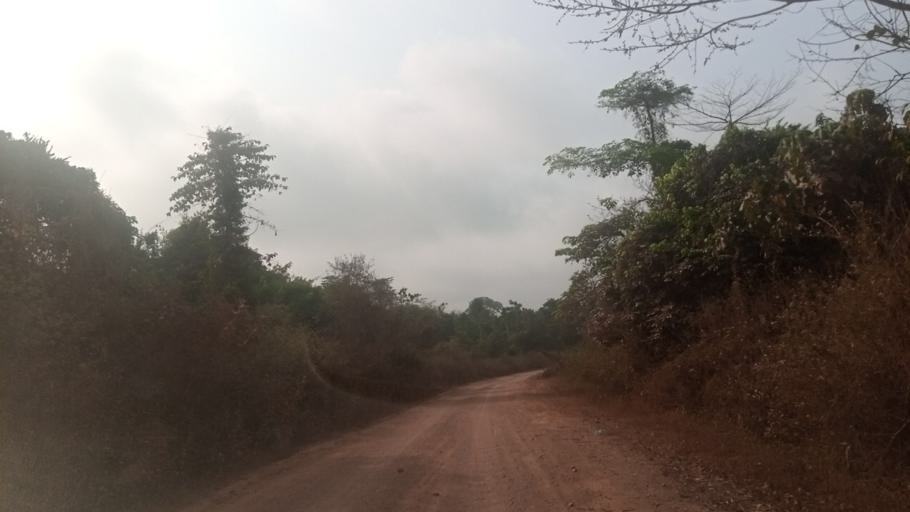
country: NG
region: Osun
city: Modakeke
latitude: 7.1240
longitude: 4.4086
